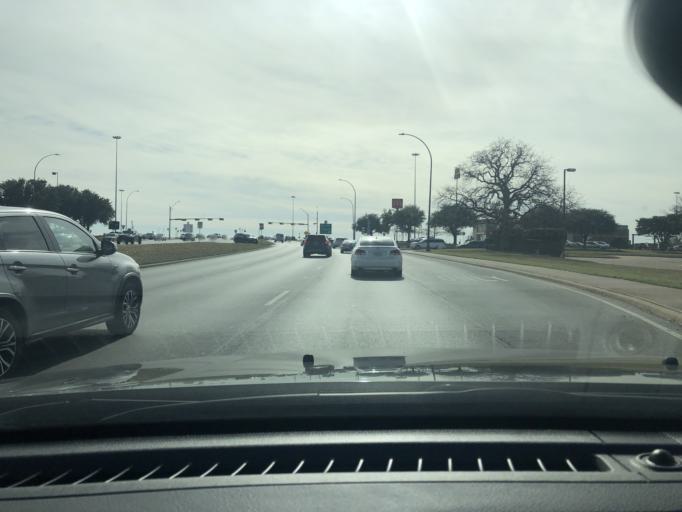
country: US
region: Texas
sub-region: Tarrant County
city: Dalworthington Gardens
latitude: 32.6787
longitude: -97.1353
